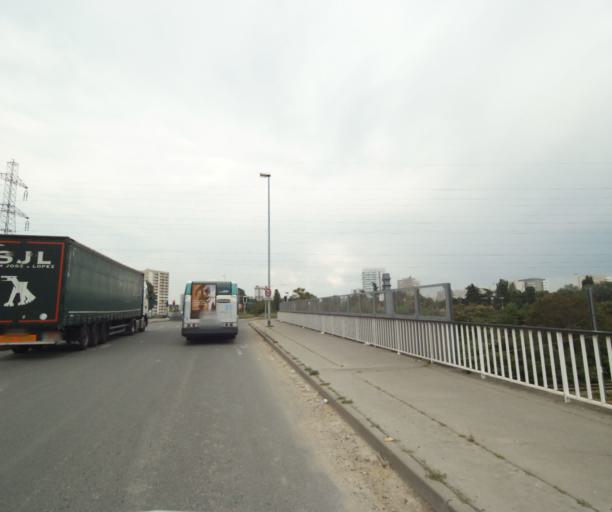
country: FR
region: Ile-de-France
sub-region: Departement des Hauts-de-Seine
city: Bois-Colombes
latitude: 48.9355
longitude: 2.2798
